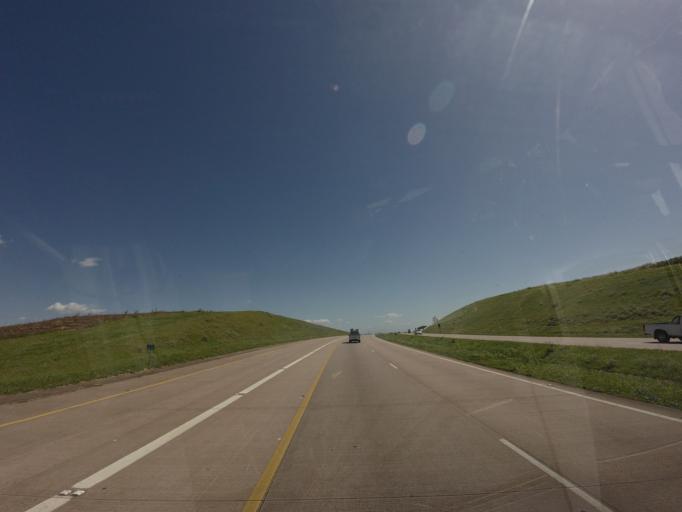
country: ZA
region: KwaZulu-Natal
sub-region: iLembe District Municipality
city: Stanger
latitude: -29.4230
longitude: 31.2735
